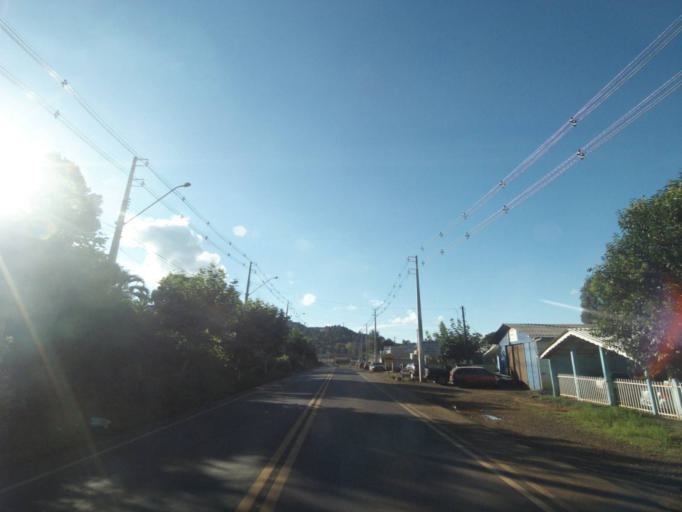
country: BR
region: Parana
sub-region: Uniao Da Vitoria
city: Uniao da Vitoria
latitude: -26.1676
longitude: -51.5331
